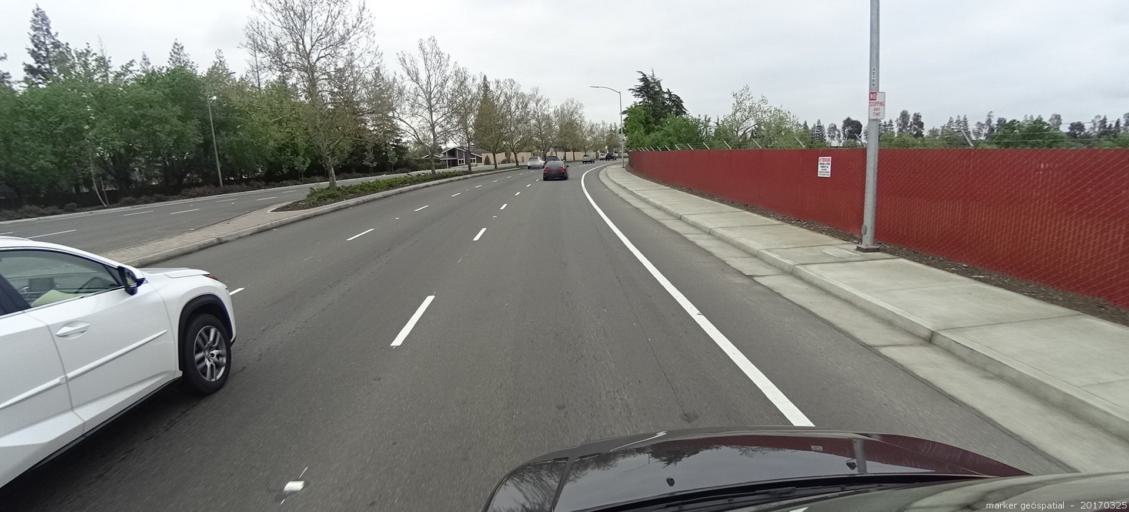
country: US
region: California
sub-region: Sacramento County
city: Rosemont
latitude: 38.5504
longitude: -121.3729
